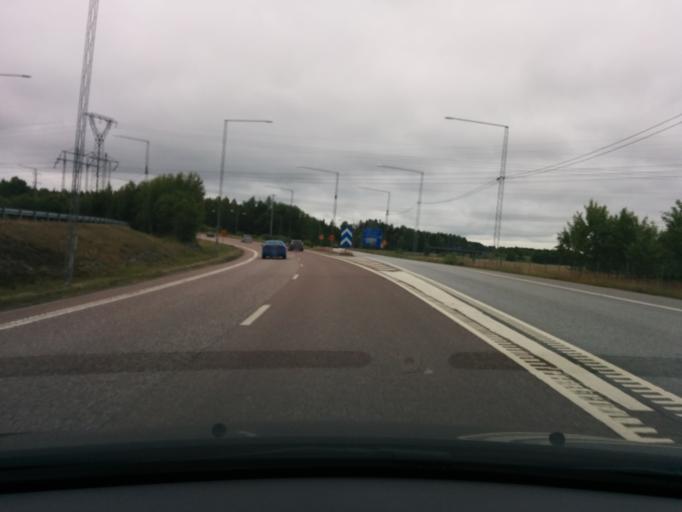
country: SE
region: Stockholm
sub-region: Sigtuna Kommun
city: Rosersberg
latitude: 59.6175
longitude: 17.8962
